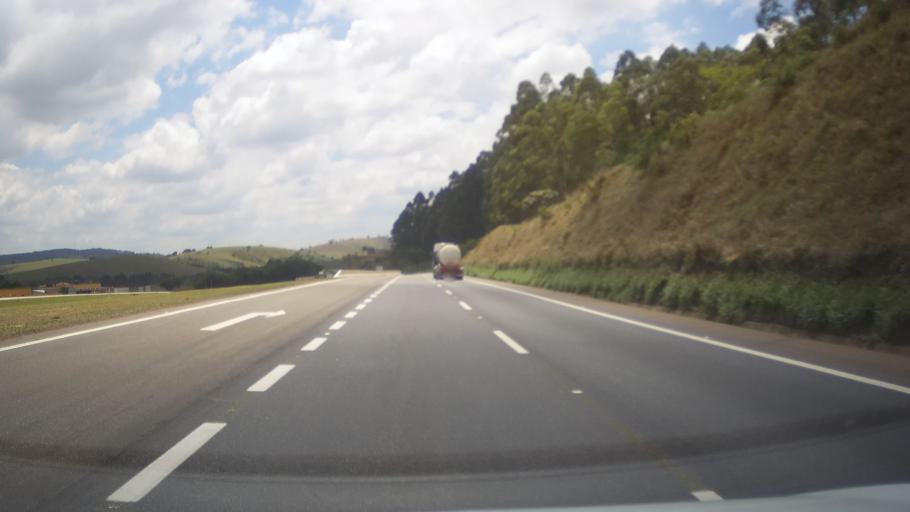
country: BR
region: Minas Gerais
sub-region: Campanha
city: Campanha
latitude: -21.7217
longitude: -45.3796
